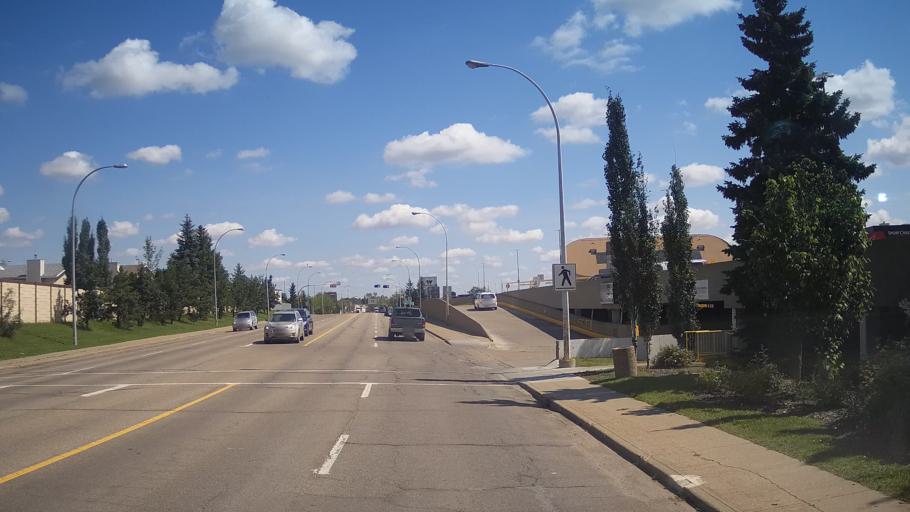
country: CA
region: Alberta
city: St. Albert
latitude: 53.5247
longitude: -113.6278
